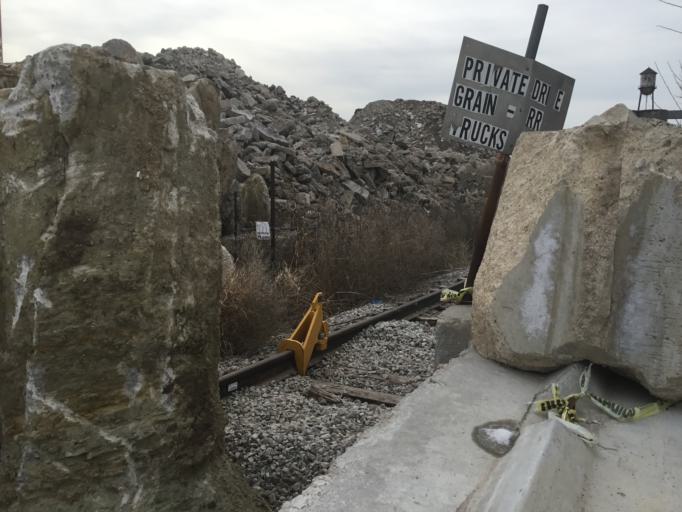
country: US
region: Kansas
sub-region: Sedgwick County
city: Wichita
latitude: 37.7208
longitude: -97.3337
